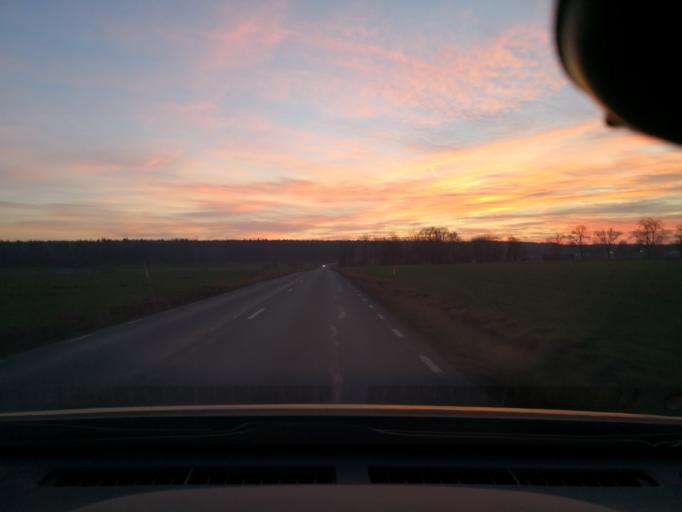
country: SE
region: OErebro
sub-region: Lindesbergs Kommun
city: Fellingsbro
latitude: 59.4281
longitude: 15.5746
